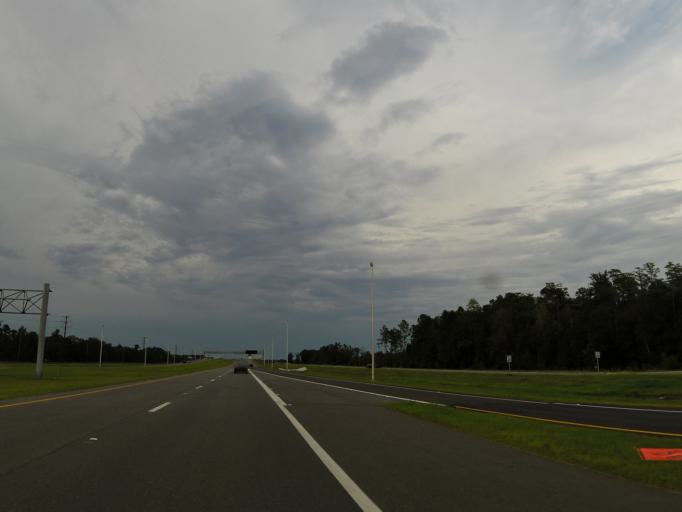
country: US
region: Florida
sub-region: Clay County
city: Lakeside
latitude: 30.1248
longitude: -81.8304
